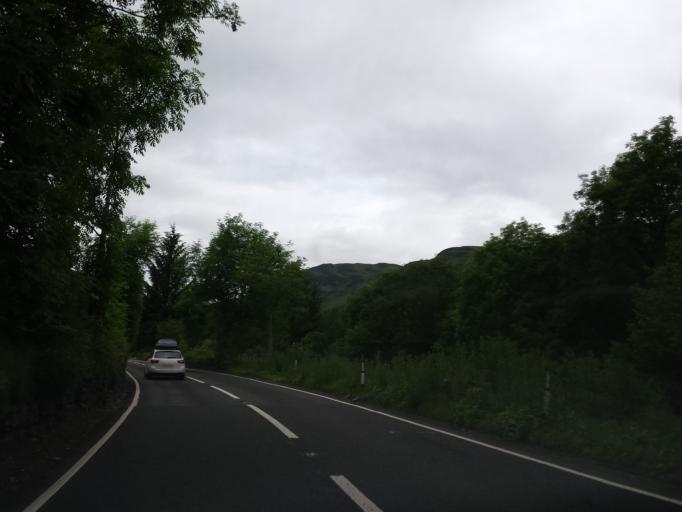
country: GB
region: Scotland
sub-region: Stirling
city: Callander
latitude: 56.3919
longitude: -4.2920
